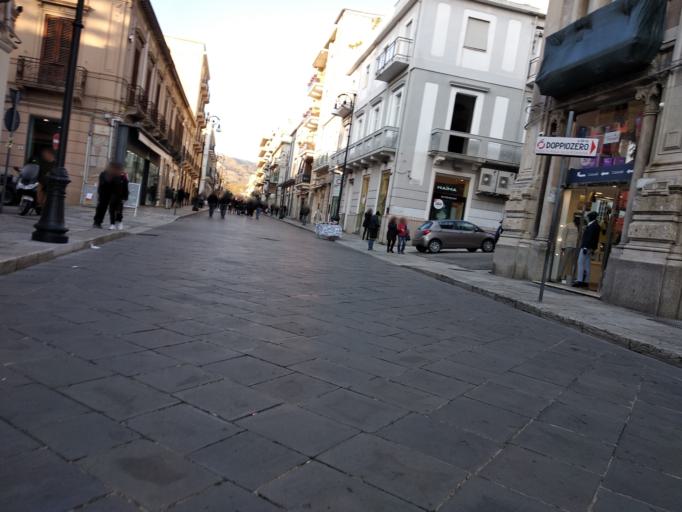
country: IT
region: Calabria
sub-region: Provincia di Reggio Calabria
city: Reggio Calabria
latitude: 38.1123
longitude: 15.6485
